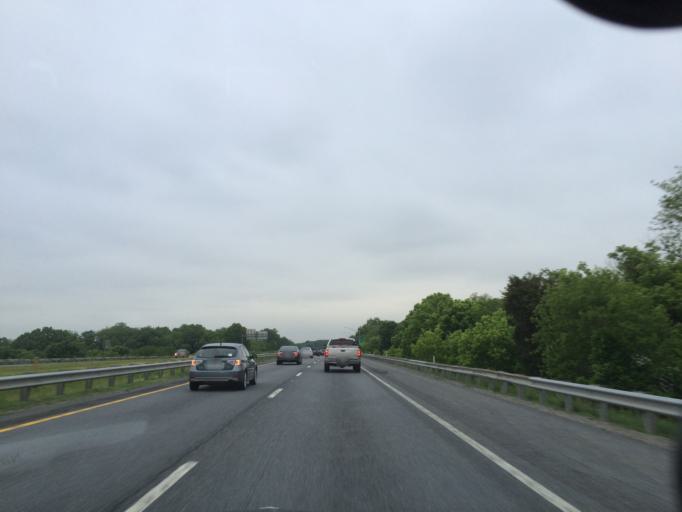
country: US
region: Maryland
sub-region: Washington County
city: Halfway
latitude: 39.6057
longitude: -77.7423
